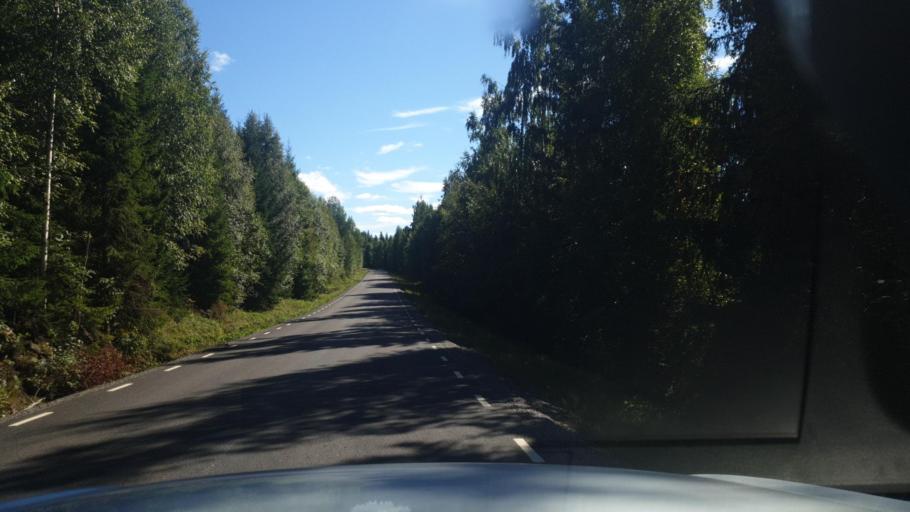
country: SE
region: Vaermland
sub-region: Torsby Kommun
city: Torsby
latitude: 59.9962
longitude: 12.7386
